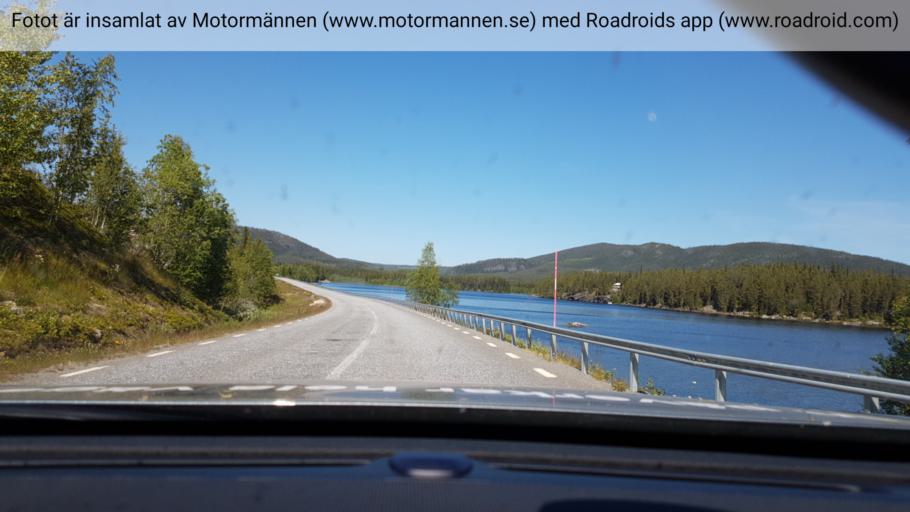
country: SE
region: Vaesterbotten
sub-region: Vilhelmina Kommun
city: Sjoberg
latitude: 64.9216
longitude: 15.8684
